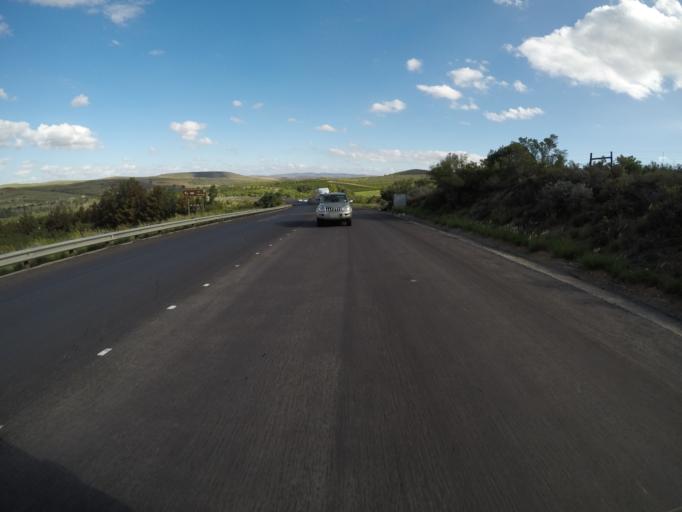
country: ZA
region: Western Cape
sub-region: Cape Winelands District Municipality
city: Ashton
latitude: -33.9439
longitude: 20.2150
